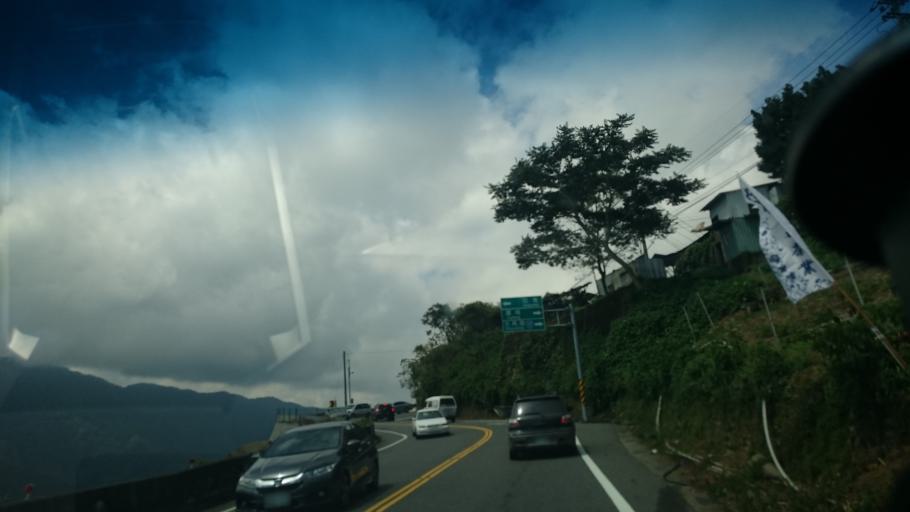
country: TW
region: Taiwan
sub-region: Nantou
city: Puli
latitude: 24.0388
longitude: 121.1449
